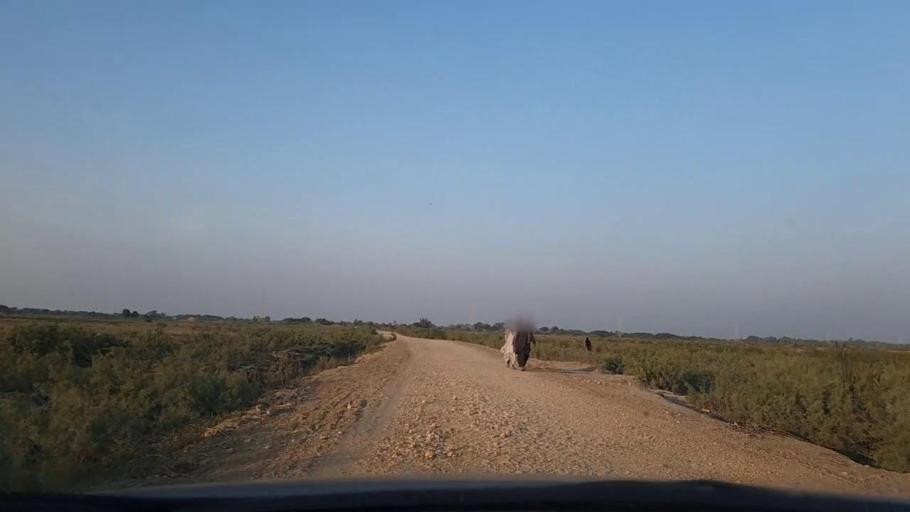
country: PK
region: Sindh
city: Mirpur Sakro
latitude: 24.5558
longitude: 67.6571
